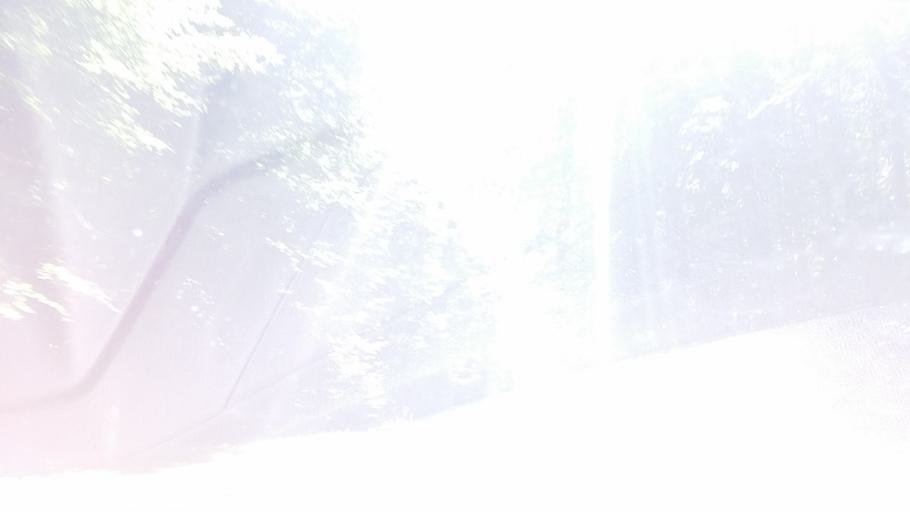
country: PL
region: West Pomeranian Voivodeship
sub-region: Powiat lobeski
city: Wegorzyno
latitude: 53.4880
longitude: 15.5813
